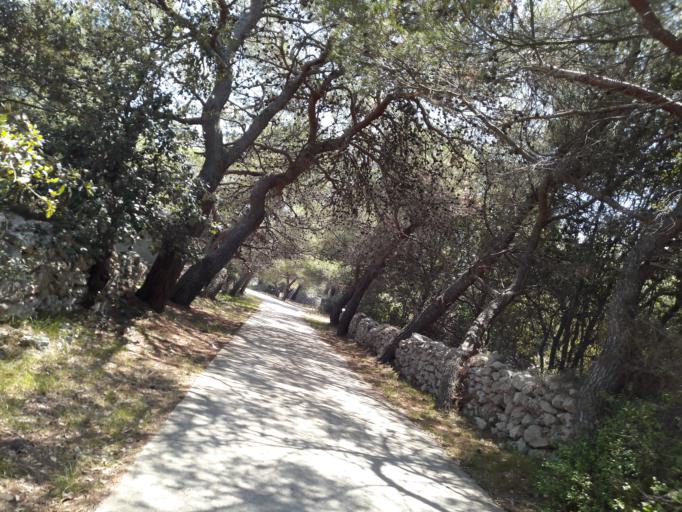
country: HR
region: Licko-Senjska
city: Novalja
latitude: 44.3700
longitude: 14.6975
